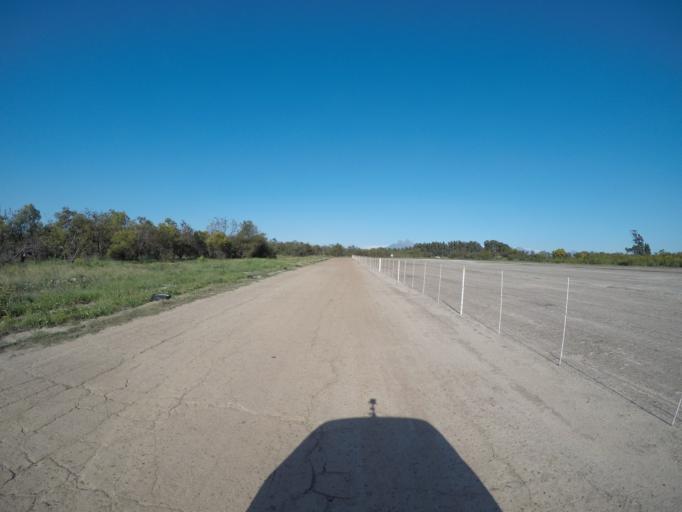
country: ZA
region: Western Cape
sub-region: City of Cape Town
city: Kraaifontein
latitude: -33.7730
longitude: 18.7455
